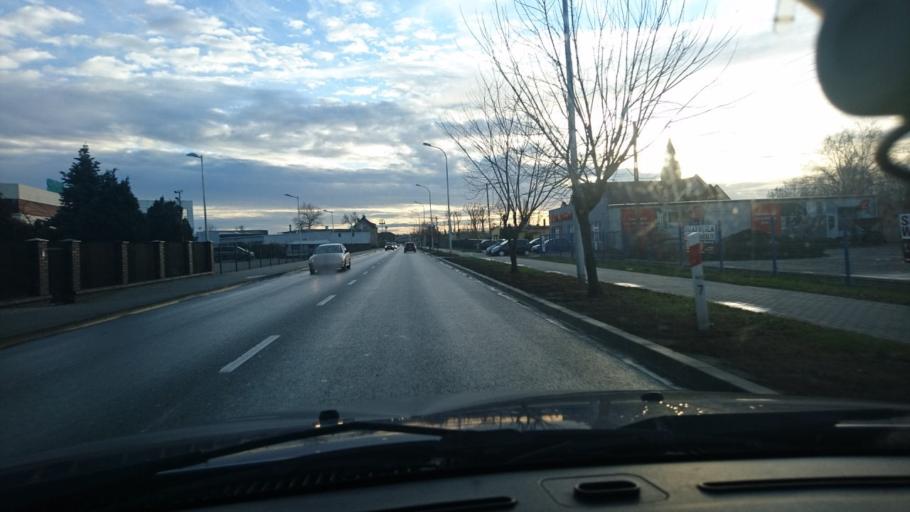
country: PL
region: Greater Poland Voivodeship
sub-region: Powiat kepinski
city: Kepno
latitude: 51.2931
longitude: 17.9954
